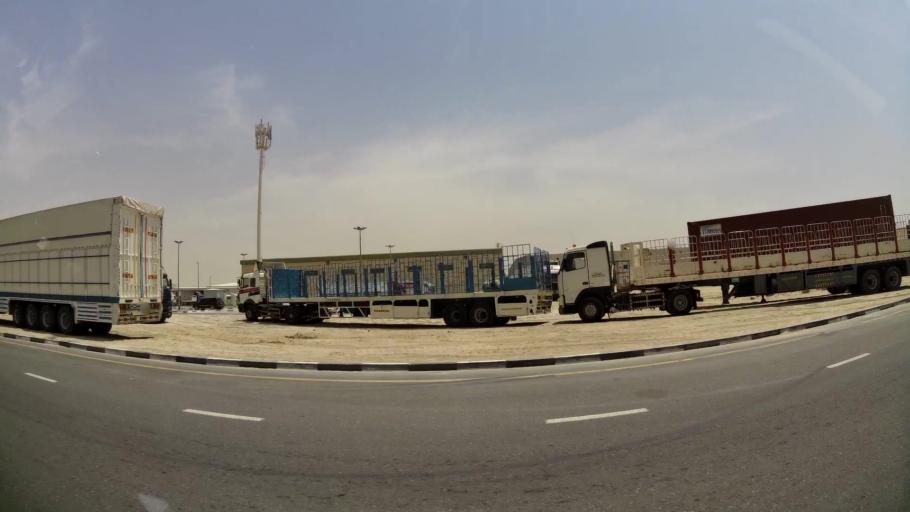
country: AE
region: Ash Shariqah
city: Sharjah
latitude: 25.1903
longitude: 55.3800
